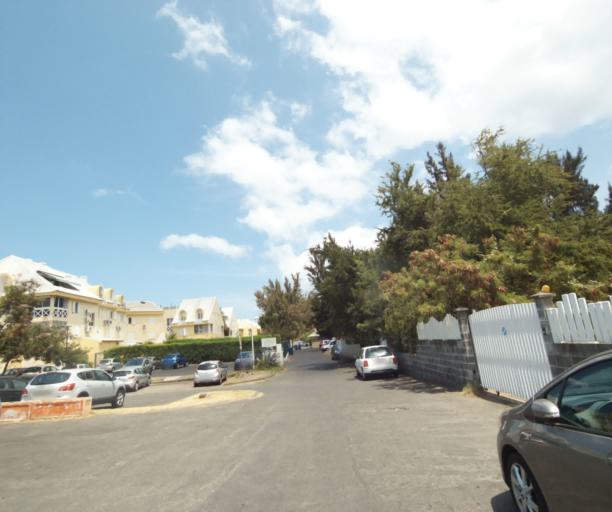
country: RE
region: Reunion
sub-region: Reunion
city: Saint-Paul
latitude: -21.0730
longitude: 55.2230
